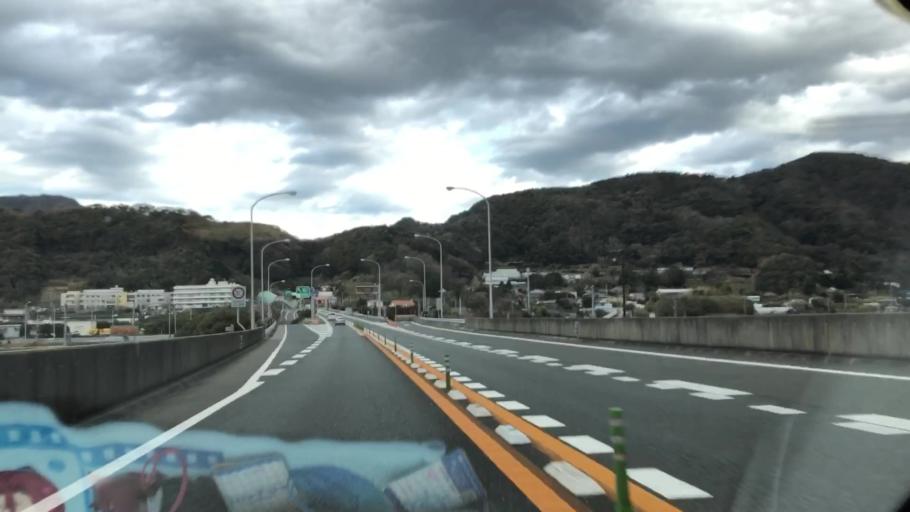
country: JP
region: Chiba
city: Tateyama
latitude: 35.1400
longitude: 139.8477
